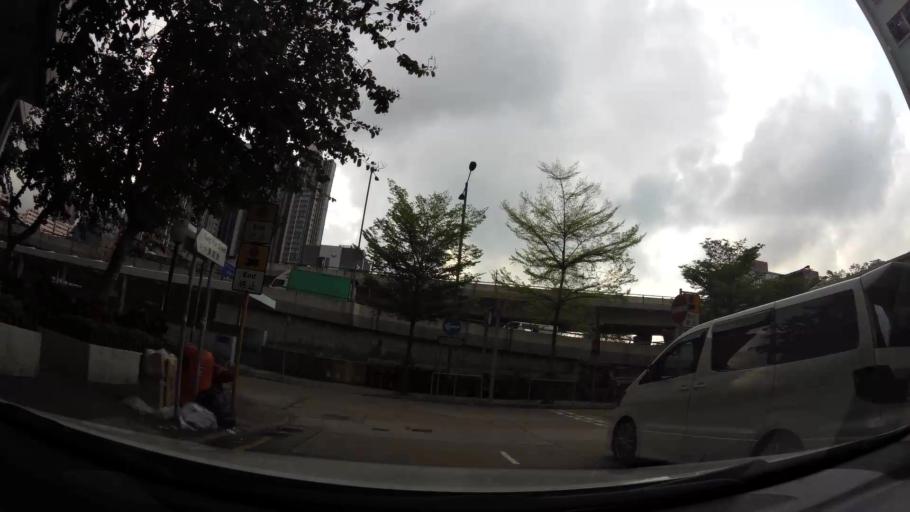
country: HK
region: Kowloon City
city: Kowloon
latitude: 22.3109
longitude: 114.1679
